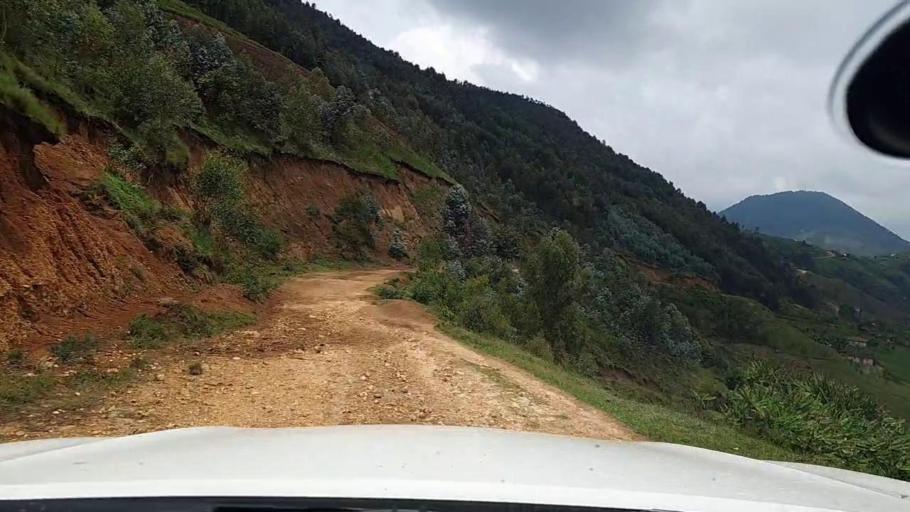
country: RW
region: Western Province
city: Kibuye
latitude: -2.1530
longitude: 29.4526
